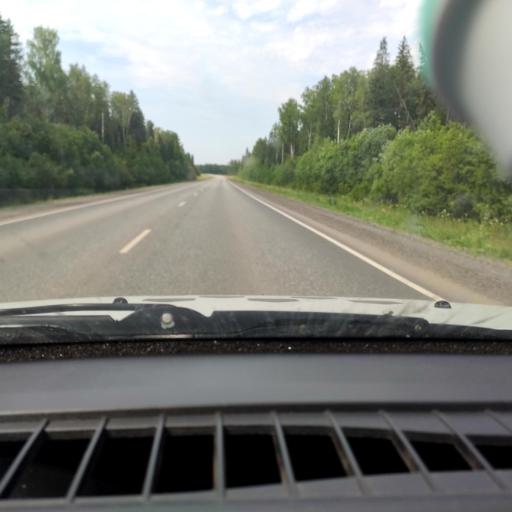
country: RU
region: Perm
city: Siva
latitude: 58.4984
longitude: 54.0465
